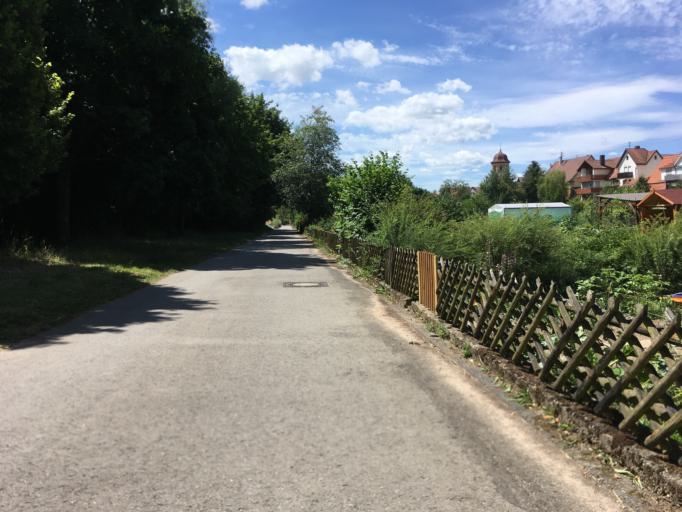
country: DE
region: Baden-Wuerttemberg
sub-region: Regierungsbezirk Stuttgart
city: Oberriexingen
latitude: 48.9277
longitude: 9.0320
